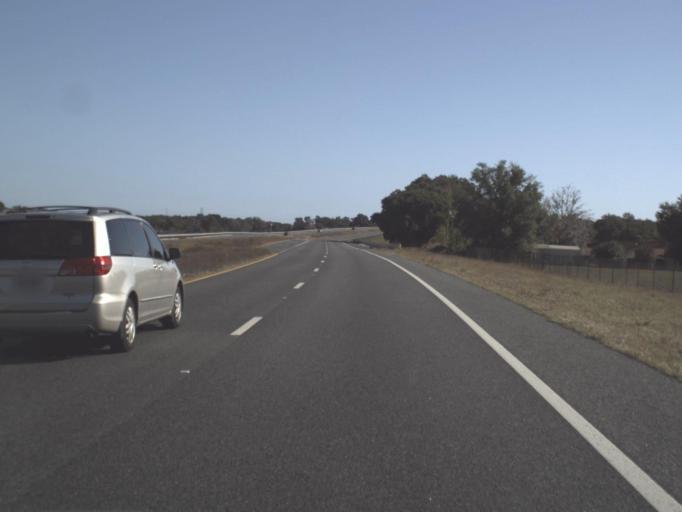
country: US
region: Florida
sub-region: Marion County
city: Belleview
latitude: 29.0293
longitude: -82.0397
